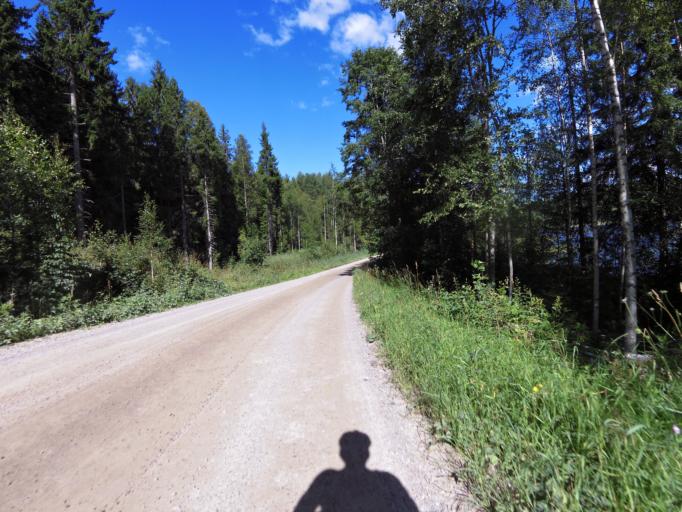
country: SE
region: Gaevleborg
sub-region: Hofors Kommun
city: Hofors
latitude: 60.4986
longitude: 16.3002
